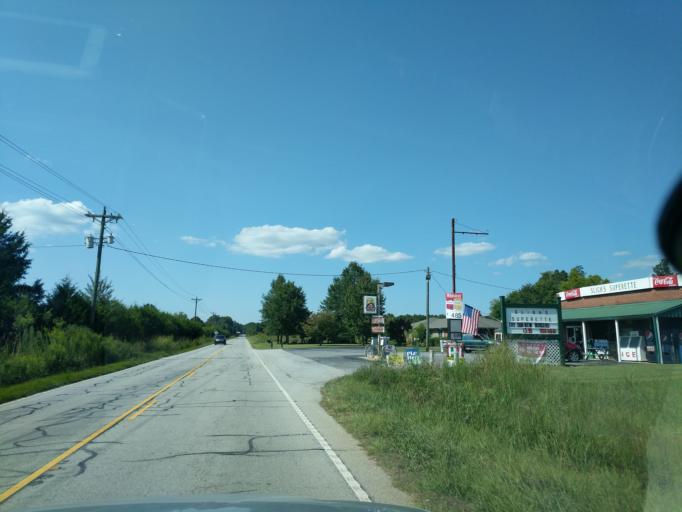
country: US
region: South Carolina
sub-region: Newberry County
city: Prosperity
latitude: 34.1553
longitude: -81.5302
